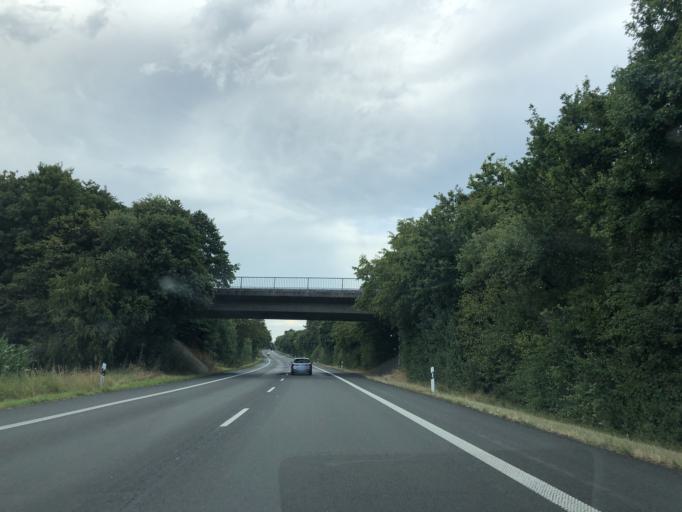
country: DE
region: North Rhine-Westphalia
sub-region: Regierungsbezirk Dusseldorf
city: Kranenburg
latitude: 51.7609
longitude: 6.0366
